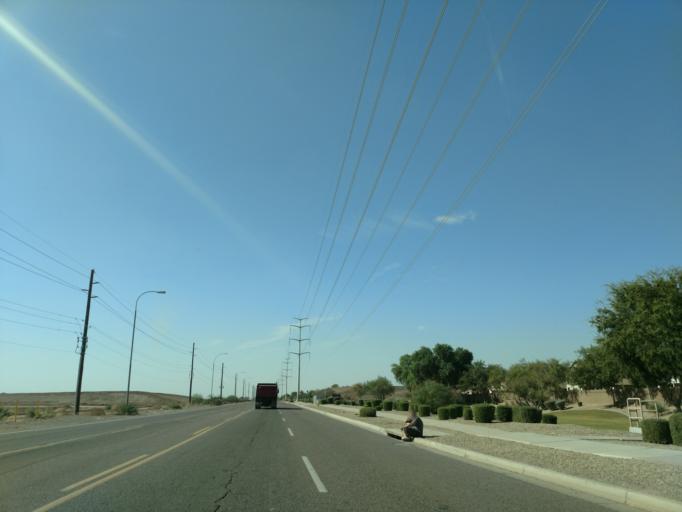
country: US
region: Arizona
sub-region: Maricopa County
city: Laveen
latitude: 33.4081
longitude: -112.1882
